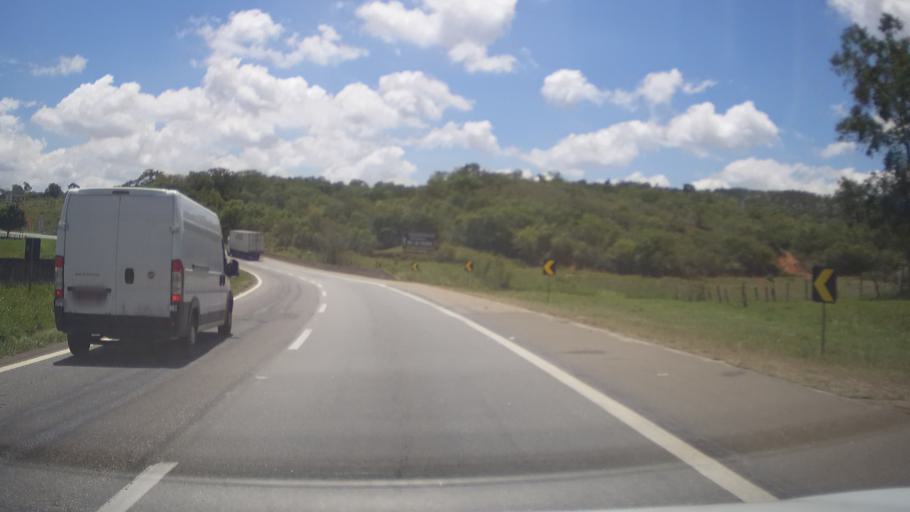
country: BR
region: Minas Gerais
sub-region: Campanha
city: Campanha
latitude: -21.8322
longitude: -45.4997
